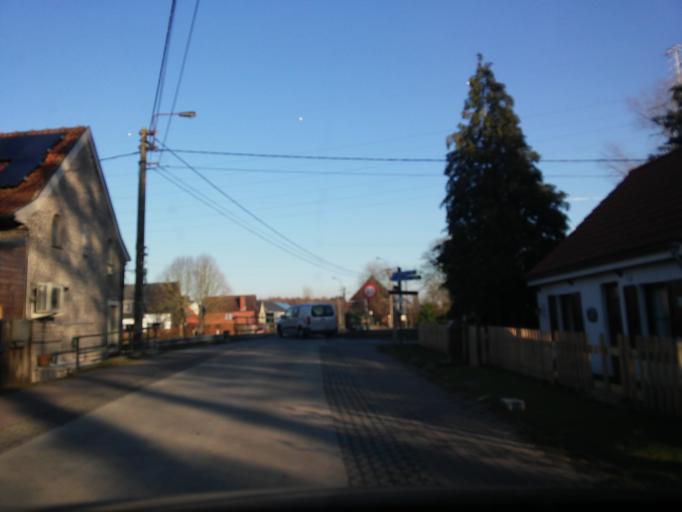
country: BE
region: Flanders
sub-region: Provincie Oost-Vlaanderen
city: Eeklo
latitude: 51.1897
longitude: 3.5257
